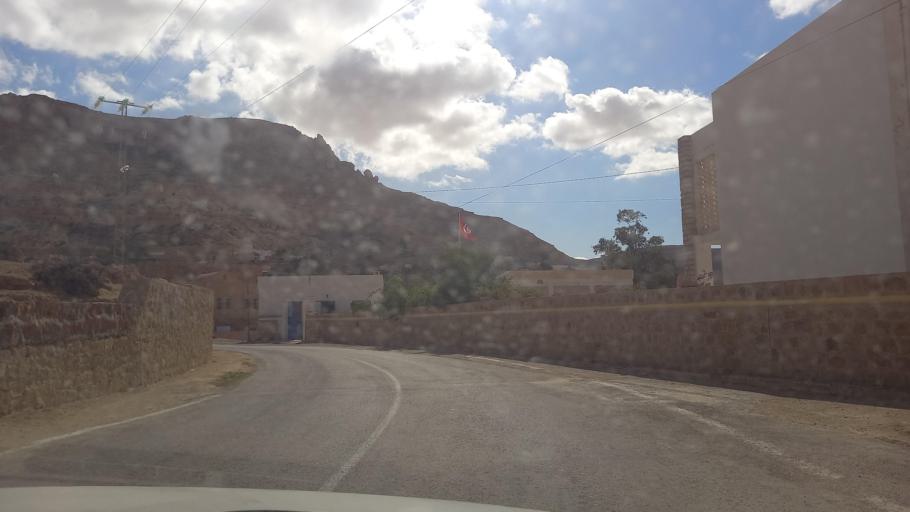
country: TN
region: Tataouine
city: Tataouine
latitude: 32.9109
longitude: 10.2597
